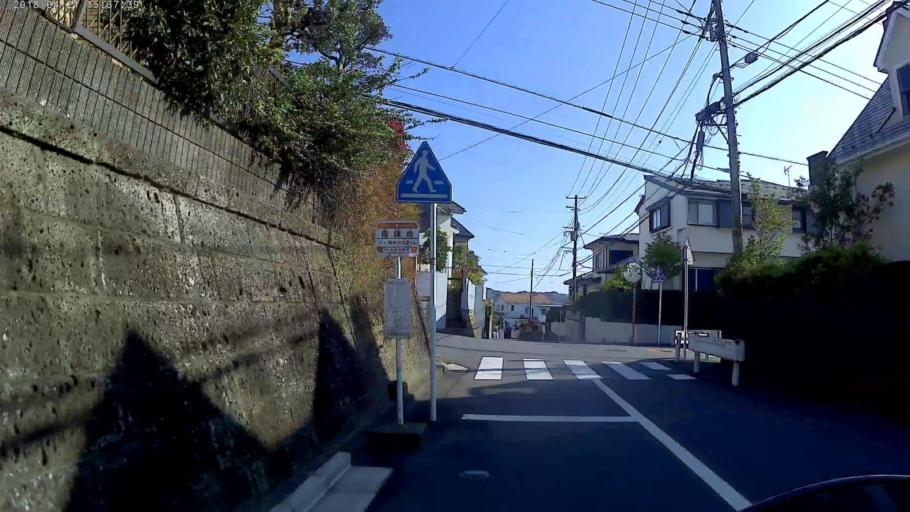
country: JP
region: Kanagawa
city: Fujisawa
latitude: 35.3191
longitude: 139.5062
